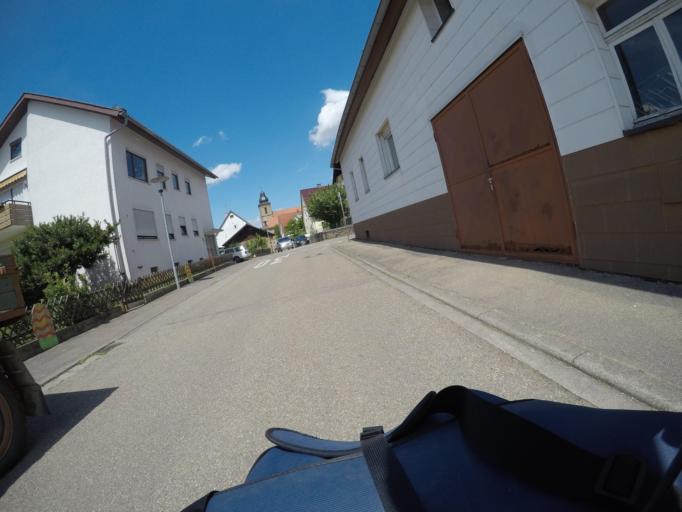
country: DE
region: Baden-Wuerttemberg
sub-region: Karlsruhe Region
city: Sinsheim
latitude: 49.2100
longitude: 8.8775
